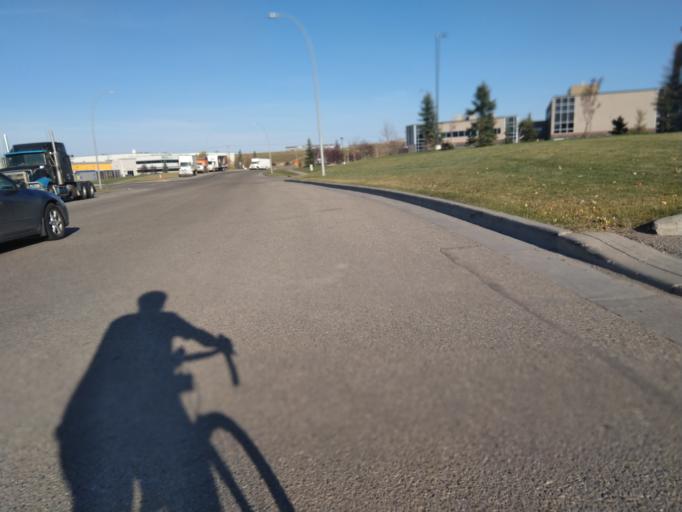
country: CA
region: Alberta
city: Calgary
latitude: 51.1055
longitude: -114.0397
